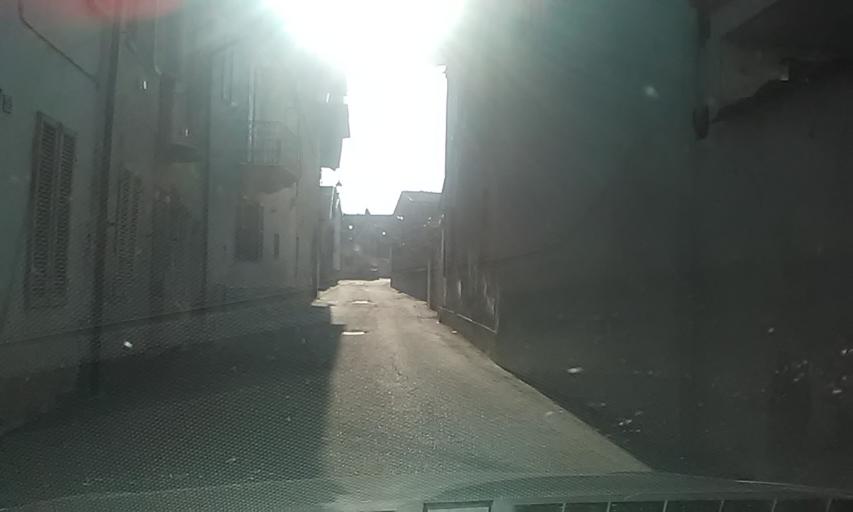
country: IT
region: Piedmont
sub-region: Provincia di Vercelli
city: Alice Castello
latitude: 45.3652
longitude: 8.0776
